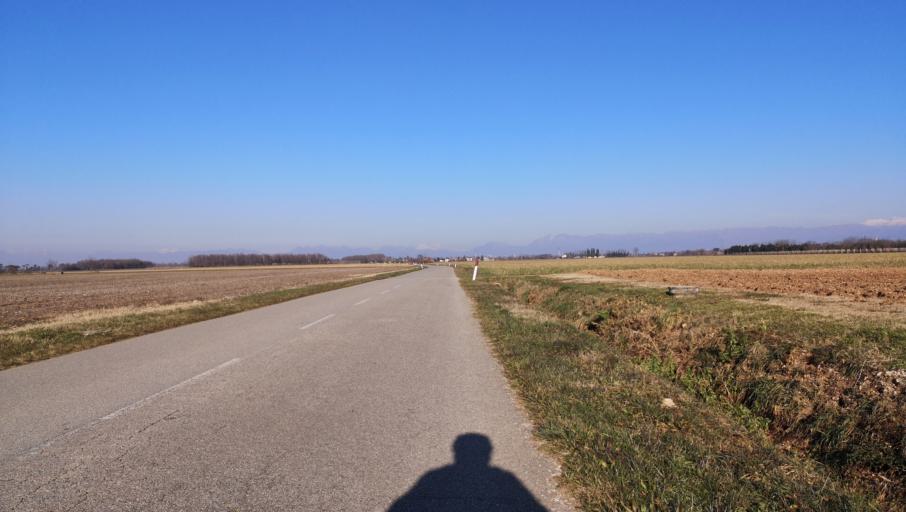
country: IT
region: Friuli Venezia Giulia
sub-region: Provincia di Udine
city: Santa Maria la Longa
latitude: 45.9399
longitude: 13.2786
